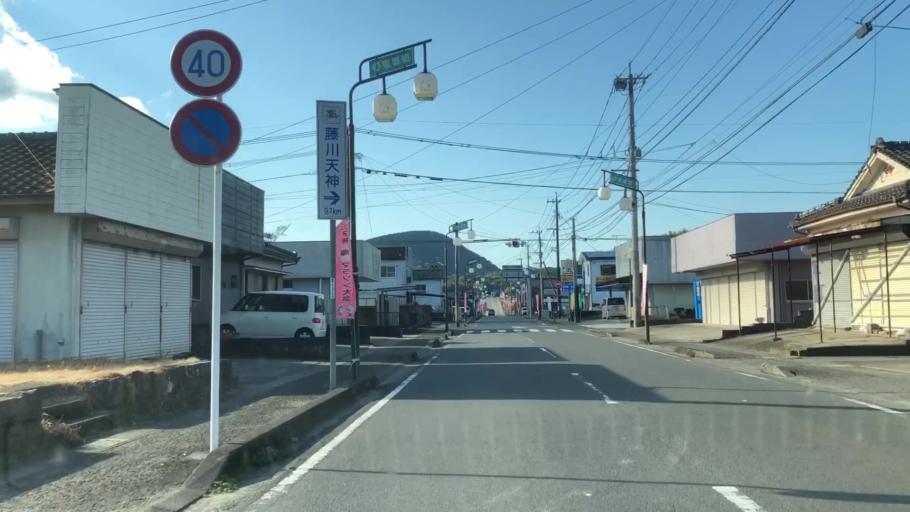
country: JP
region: Kagoshima
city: Satsumasendai
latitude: 31.8636
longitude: 130.3351
